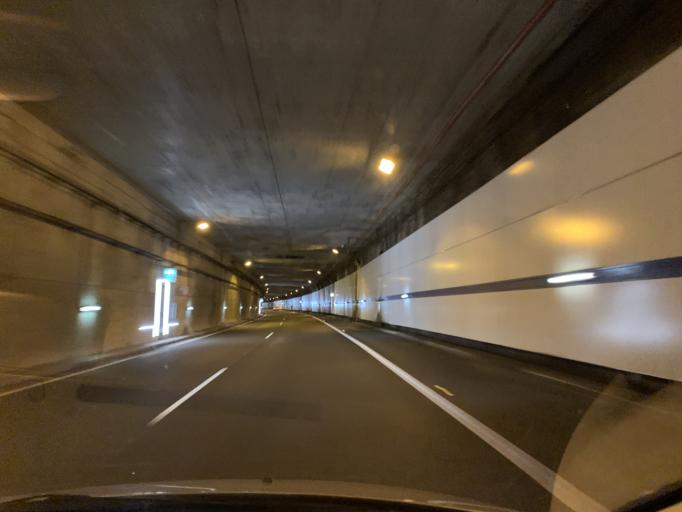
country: ES
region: Asturias
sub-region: Province of Asturias
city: Villaviciosa
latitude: 43.4868
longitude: -5.4370
